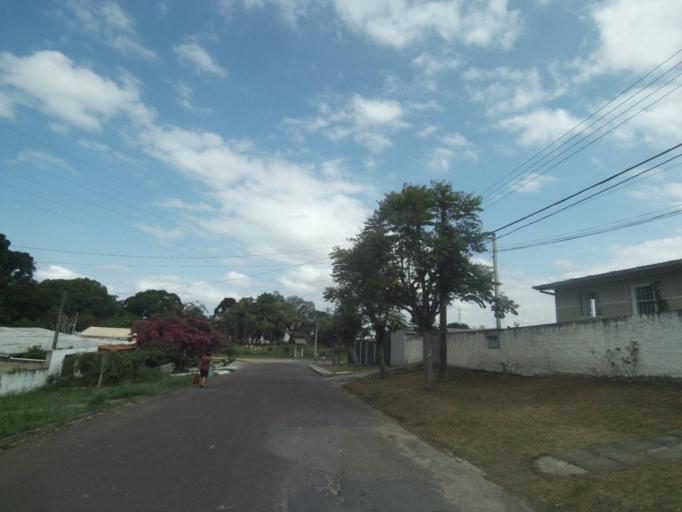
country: BR
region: Parana
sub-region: Pinhais
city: Pinhais
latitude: -25.4082
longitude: -49.1967
